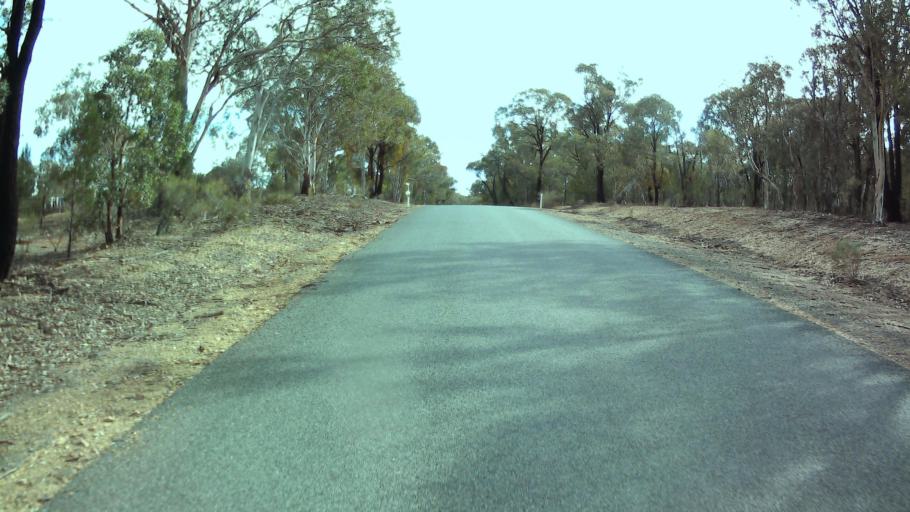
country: AU
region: New South Wales
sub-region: Weddin
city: Grenfell
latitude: -33.8874
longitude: 148.1962
